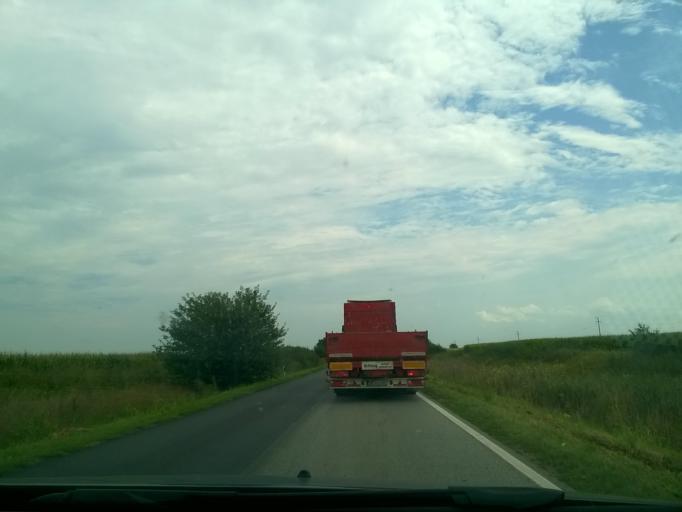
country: RS
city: Klek
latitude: 45.3841
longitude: 20.4519
